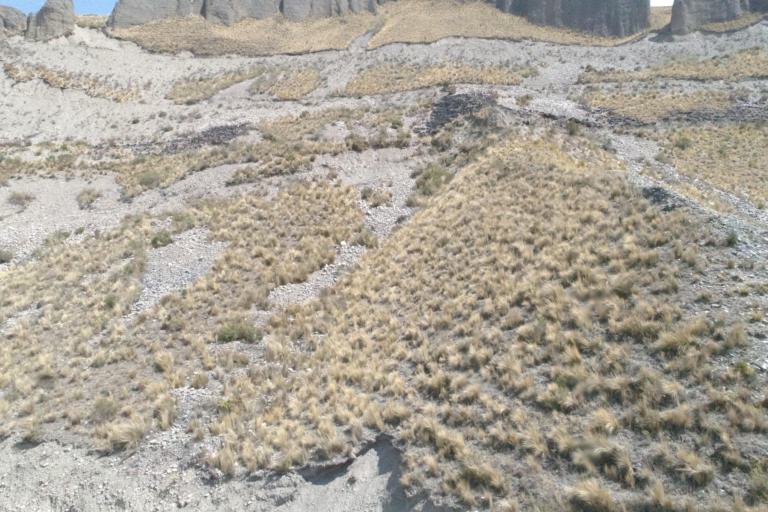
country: BO
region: La Paz
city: La Paz
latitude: -16.4727
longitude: -68.0983
